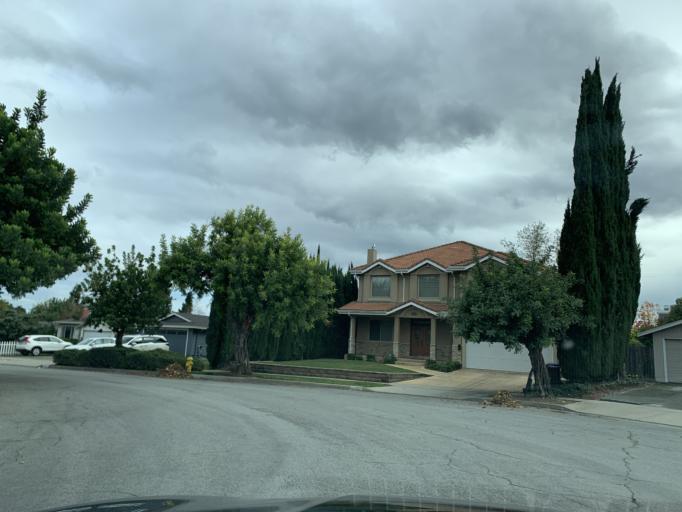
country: US
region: California
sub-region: Santa Clara County
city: Monte Sereno
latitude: 37.2687
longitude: -121.9847
